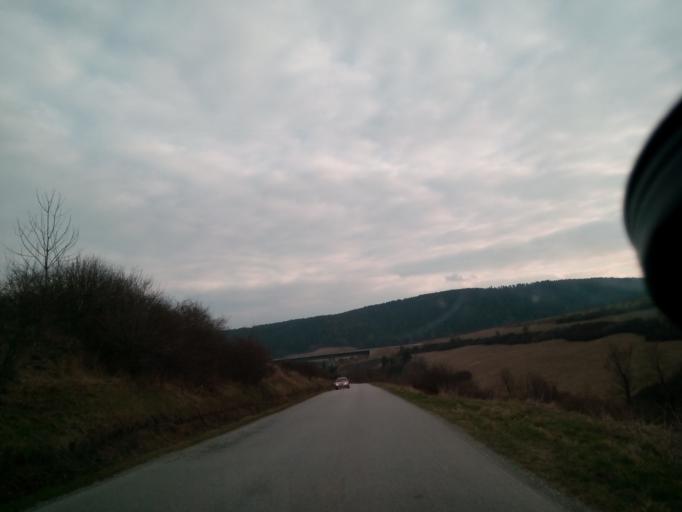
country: SK
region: Presovsky
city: Sabinov
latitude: 49.0335
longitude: 21.0188
